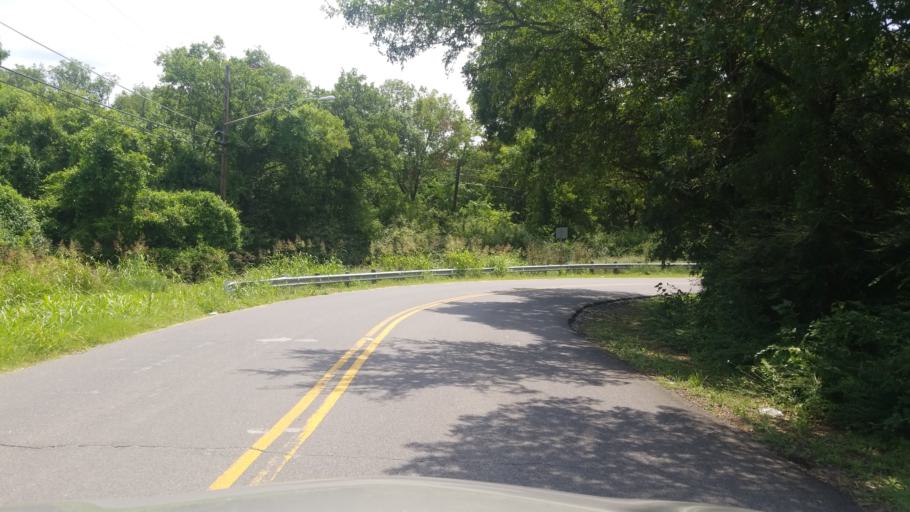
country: US
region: Texas
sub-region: Dallas County
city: Duncanville
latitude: 32.6863
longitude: -96.9345
